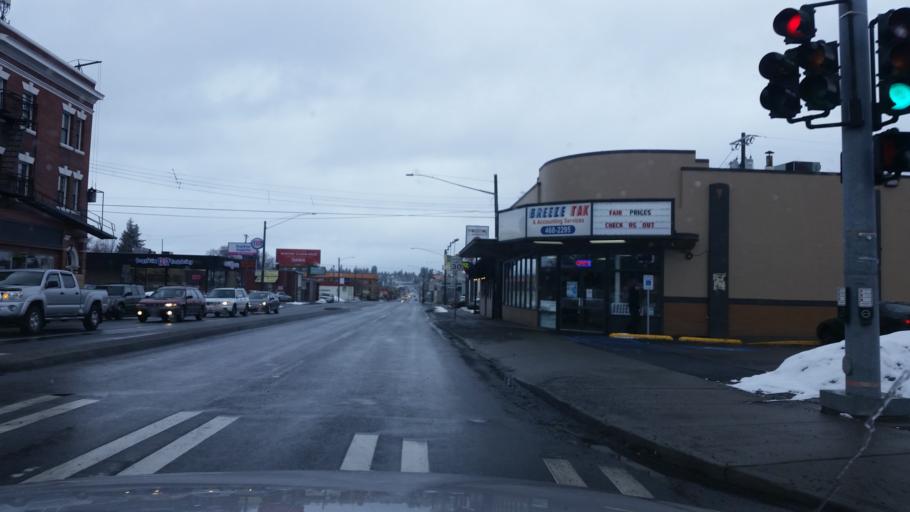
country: US
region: Washington
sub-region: Spokane County
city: Spokane
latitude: 47.6750
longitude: -117.4266
